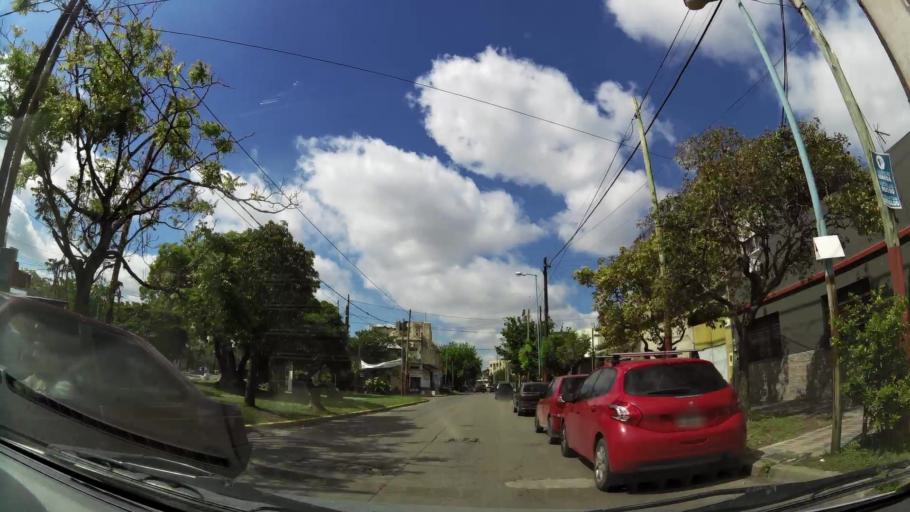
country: AR
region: Buenos Aires
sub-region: Partido de Lanus
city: Lanus
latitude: -34.6795
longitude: -58.4212
